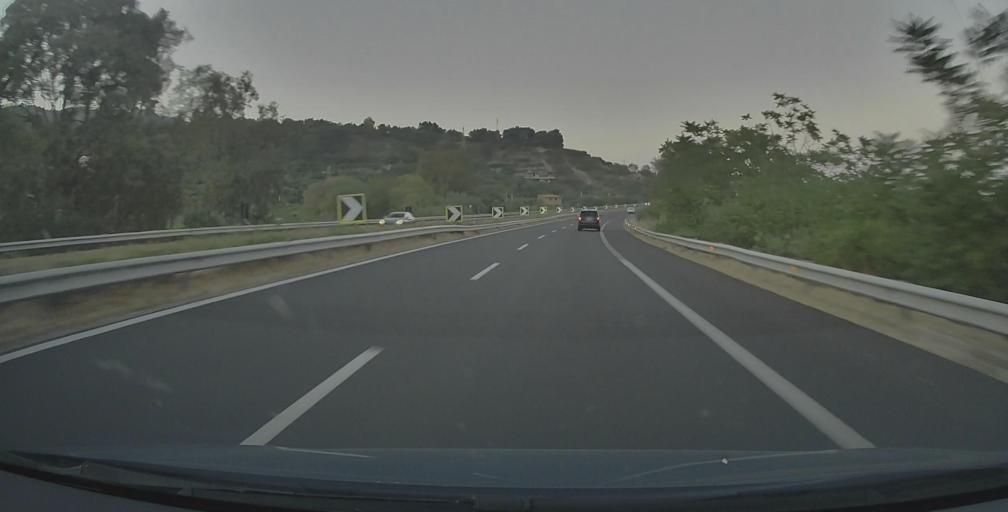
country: IT
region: Sicily
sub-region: Messina
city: Nizza di Sicilia
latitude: 37.9992
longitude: 15.4136
